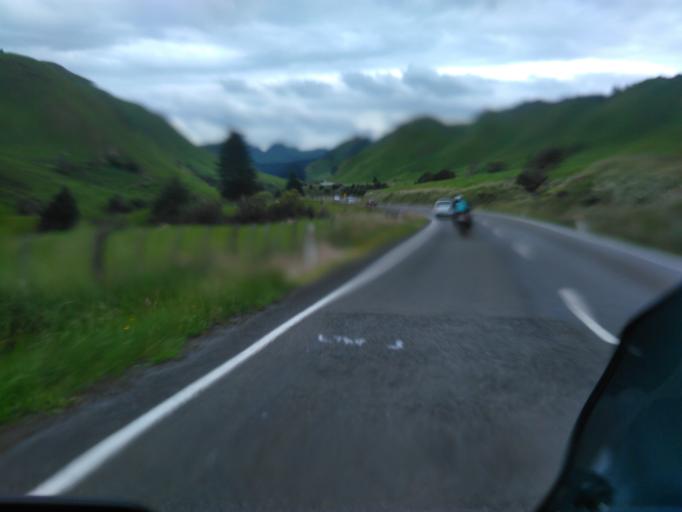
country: NZ
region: Bay of Plenty
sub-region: Opotiki District
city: Opotiki
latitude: -38.3638
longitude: 177.4623
